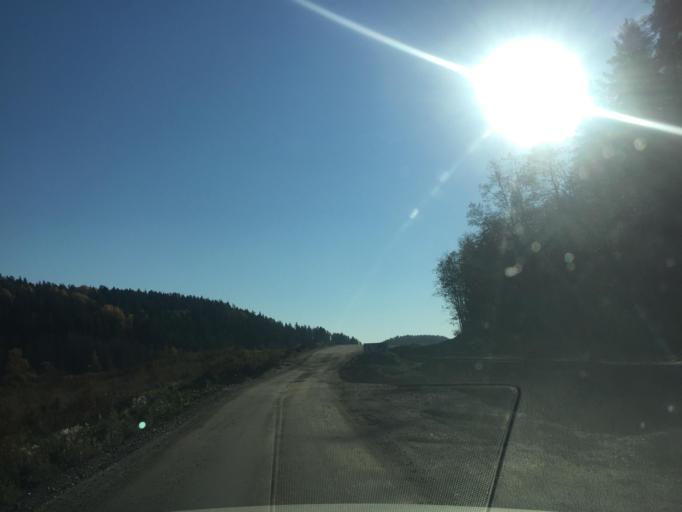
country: RU
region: Leningrad
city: Kuznechnoye
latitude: 61.3228
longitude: 29.8667
